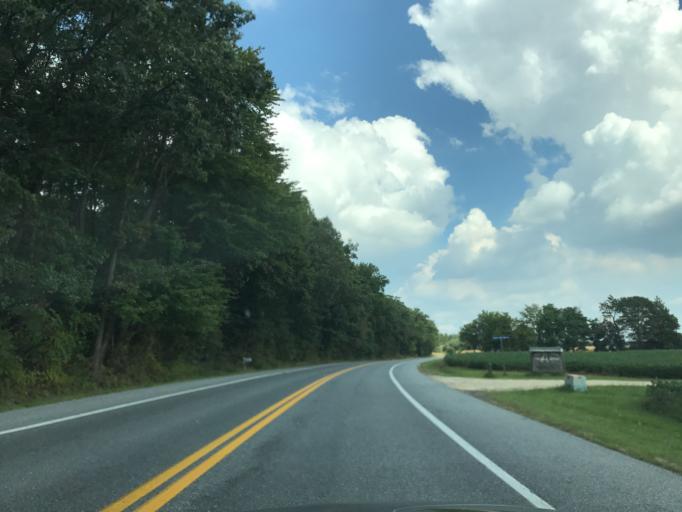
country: US
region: Delaware
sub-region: Kent County
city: Clayton
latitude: 39.1953
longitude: -75.7604
